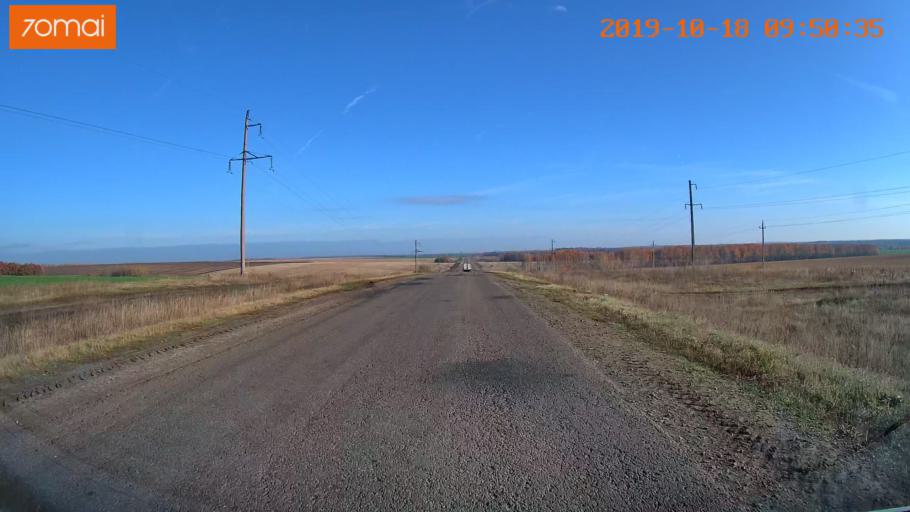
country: RU
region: Tula
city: Kazachka
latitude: 53.3304
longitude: 38.2794
